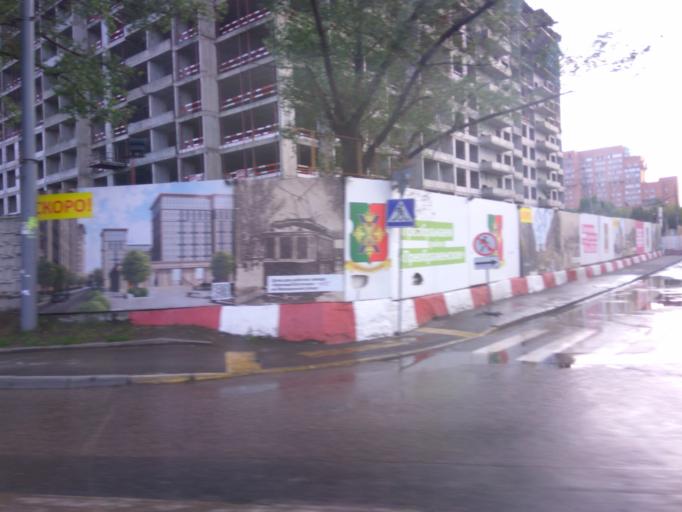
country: RU
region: Moskovskaya
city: Bogorodskoye
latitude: 55.8015
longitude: 37.7109
